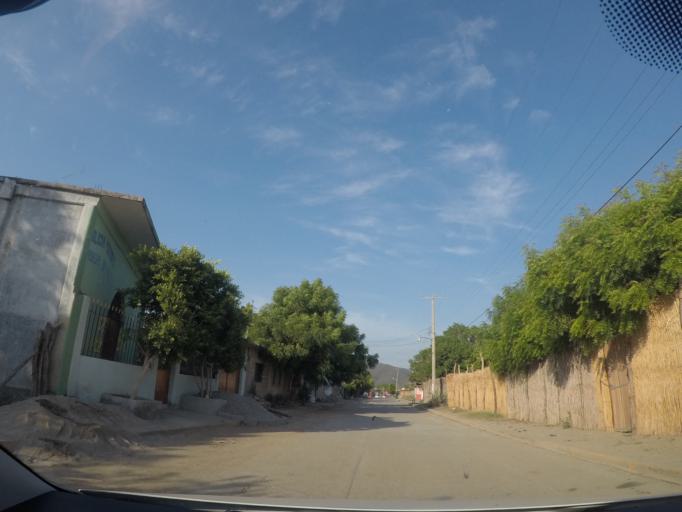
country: MX
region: Oaxaca
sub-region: Santo Domingo Tehuantepec
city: La Noria
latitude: 16.2472
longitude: -95.1506
